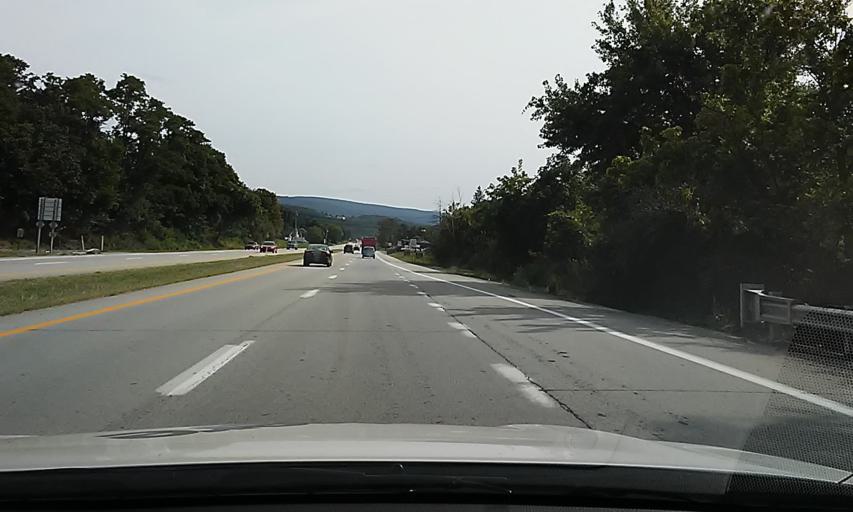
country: US
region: Pennsylvania
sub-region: Westmoreland County
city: Scottdale
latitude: 40.0704
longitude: -79.5653
